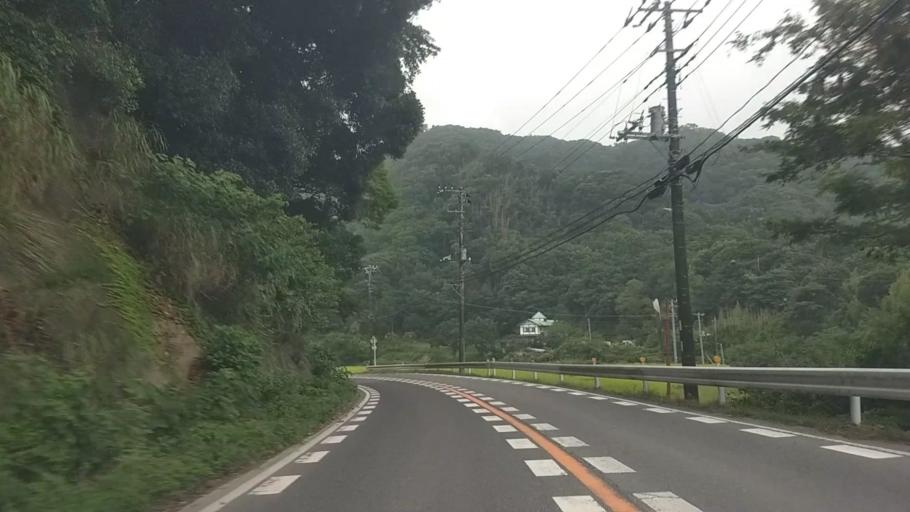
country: JP
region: Chiba
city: Tateyama
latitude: 35.1442
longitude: 139.8719
